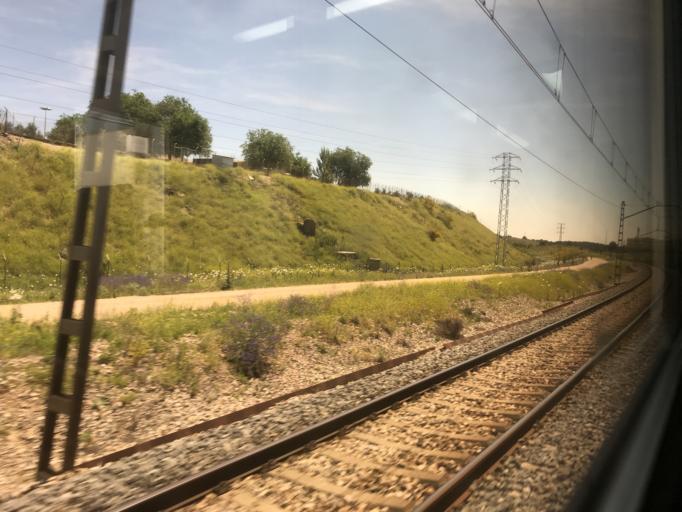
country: ES
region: Madrid
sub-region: Provincia de Madrid
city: Valdemoro
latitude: 40.2135
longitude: -3.6799
